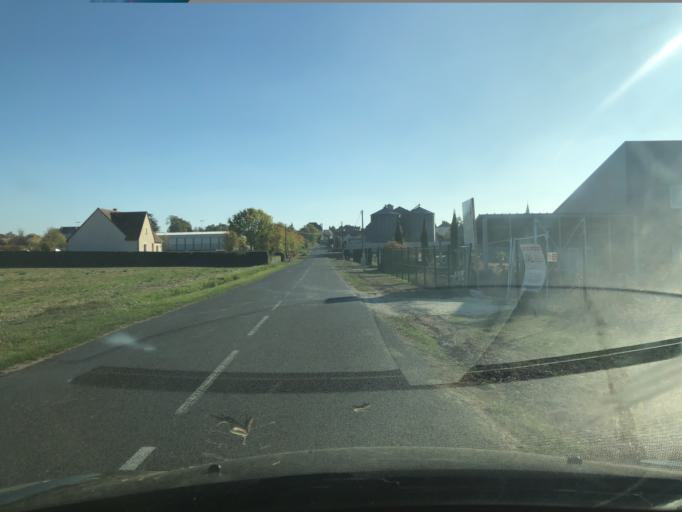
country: FR
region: Centre
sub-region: Departement d'Indre-et-Loire
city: Neuvy-le-Roi
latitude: 47.6088
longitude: 0.5968
